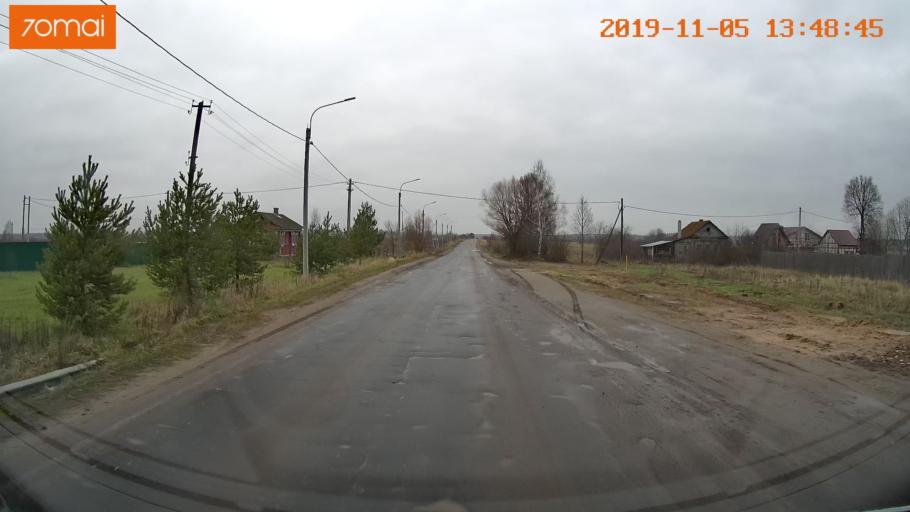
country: RU
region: Ivanovo
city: Shuya
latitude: 57.0050
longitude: 41.4073
